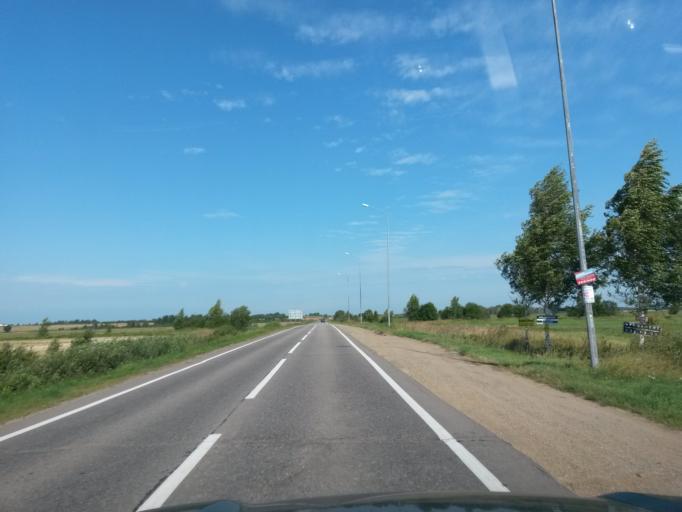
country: RU
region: Jaroslavl
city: Yaroslavl
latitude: 57.7420
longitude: 39.8890
